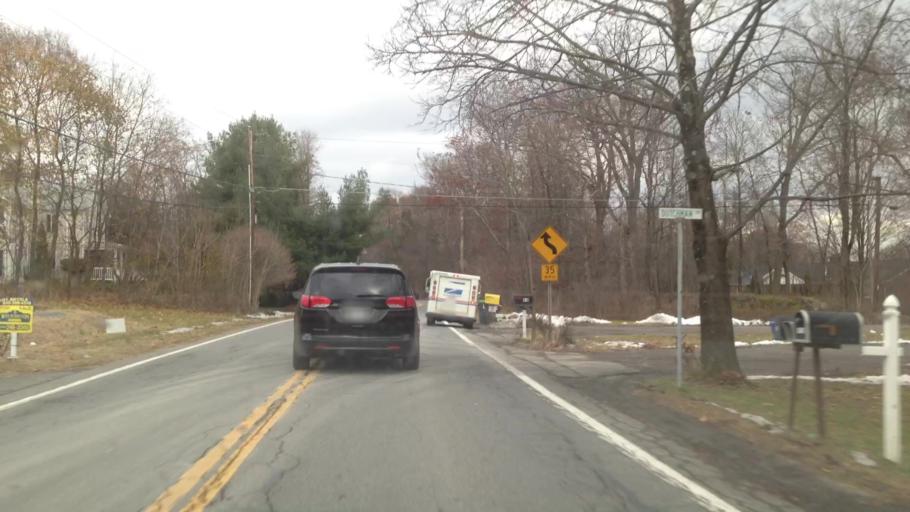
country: US
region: New York
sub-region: Ulster County
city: Glasco
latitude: 42.0168
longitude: -73.9595
